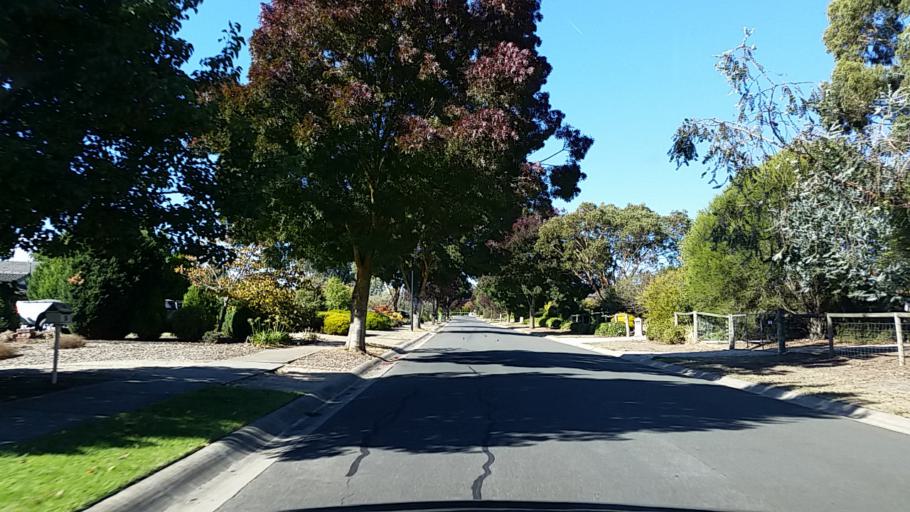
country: AU
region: South Australia
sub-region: Mount Barker
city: Mount Barker
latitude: -35.0591
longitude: 138.8773
